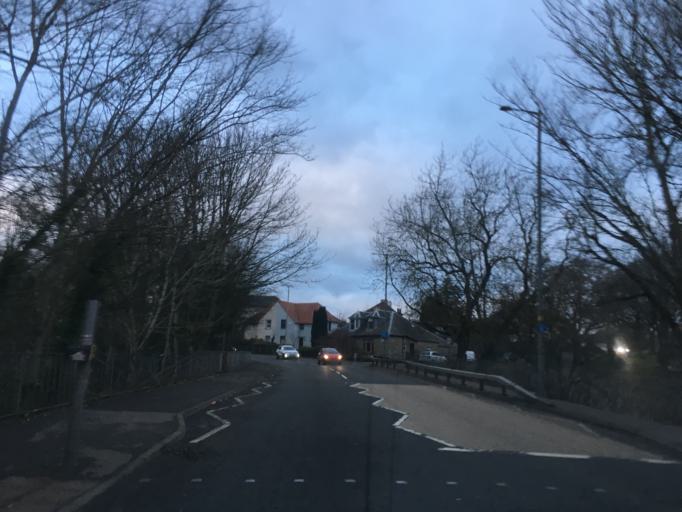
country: GB
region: Scotland
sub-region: Stirling
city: Bannockburn
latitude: 56.0923
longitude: -3.9153
